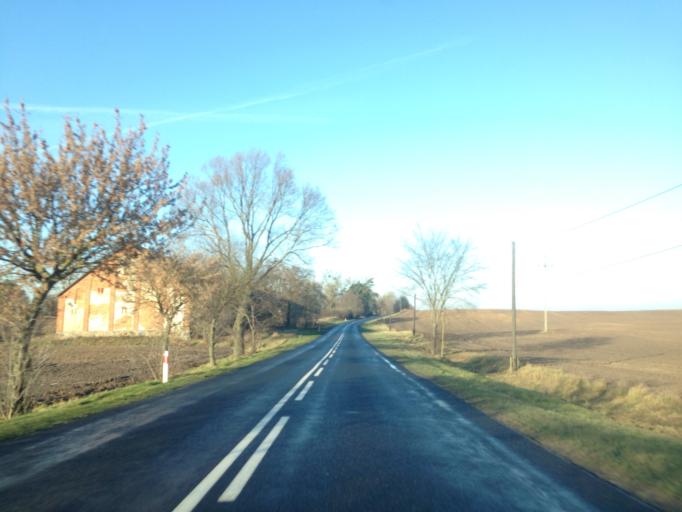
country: PL
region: Kujawsko-Pomorskie
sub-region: Powiat brodnicki
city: Bobrowo
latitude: 53.3310
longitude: 19.2335
